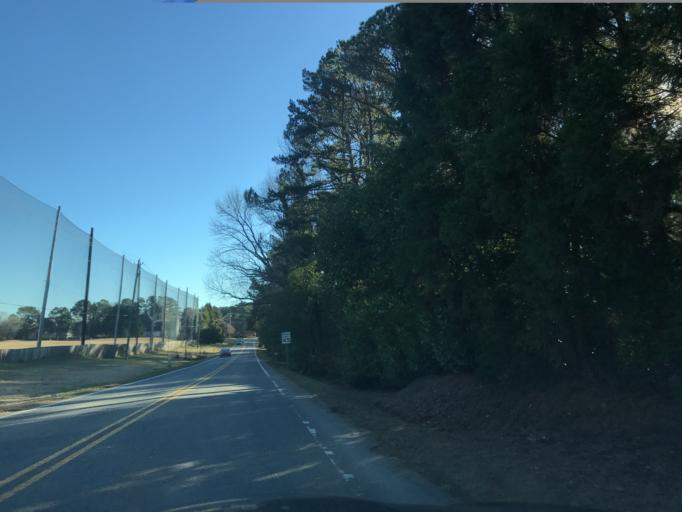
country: US
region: North Carolina
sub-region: Wake County
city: West Raleigh
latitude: 35.9054
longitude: -78.6934
